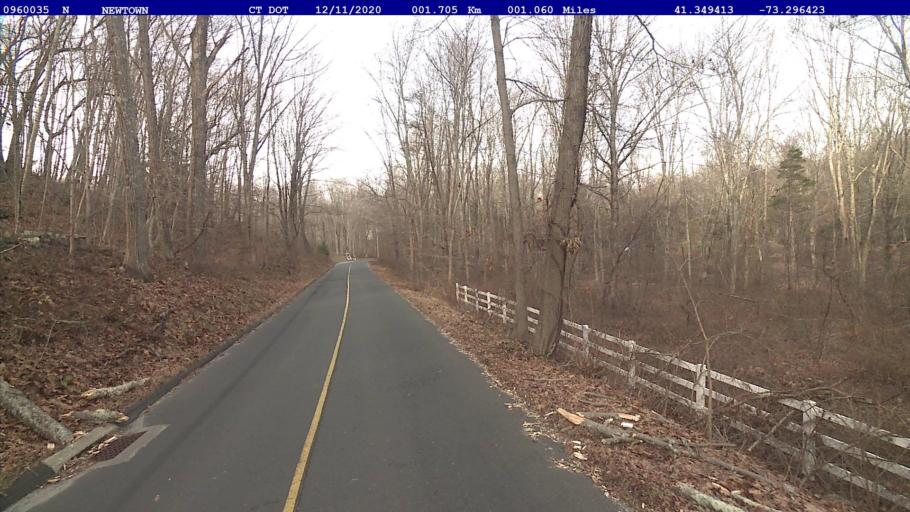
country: US
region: Connecticut
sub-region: Fairfield County
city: Newtown
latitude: 41.3494
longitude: -73.2964
